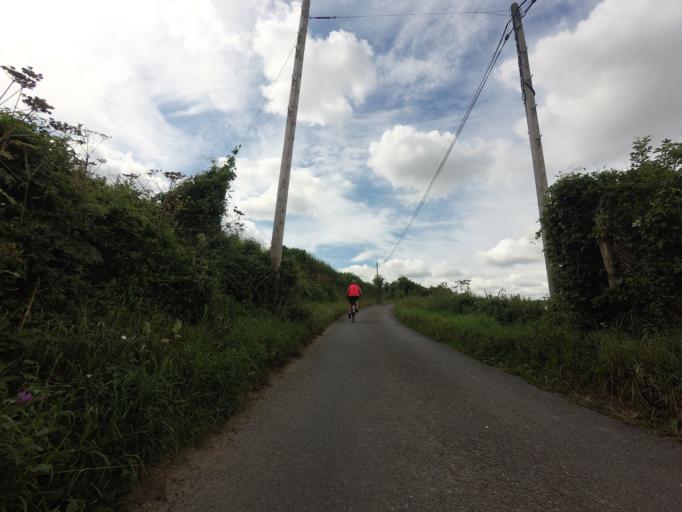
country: GB
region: England
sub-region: Kent
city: Swanley
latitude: 51.3719
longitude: 0.1415
